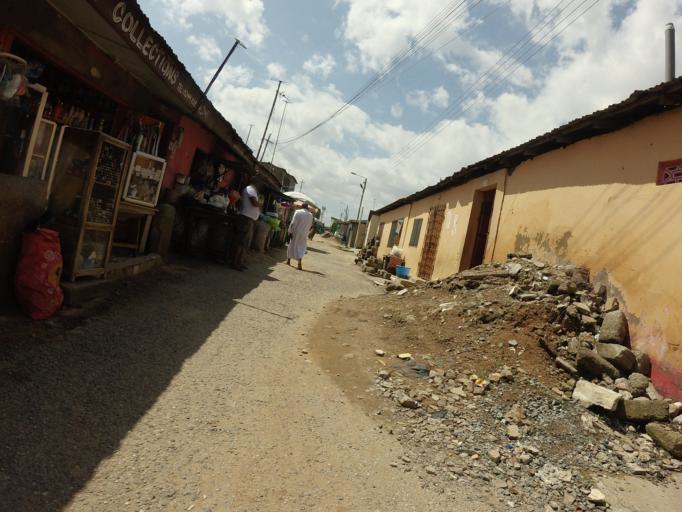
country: GH
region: Greater Accra
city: Accra
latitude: 5.5823
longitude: -0.1956
